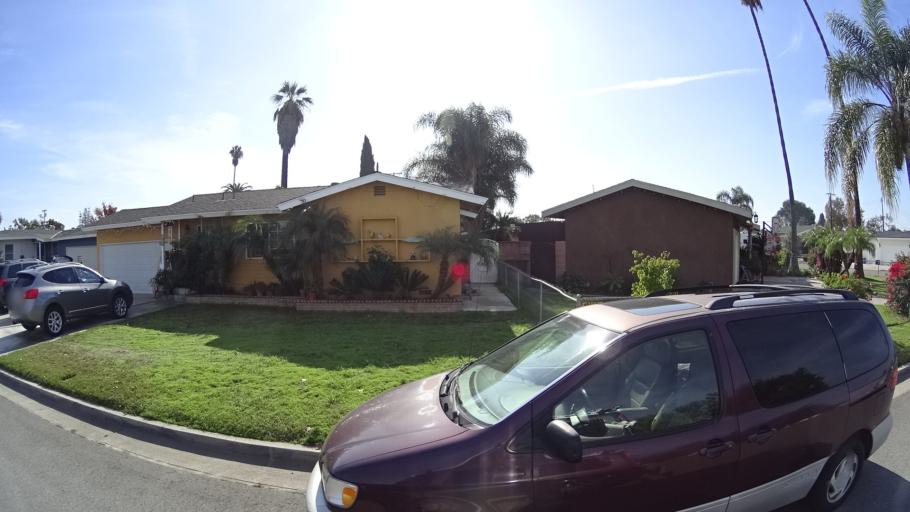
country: US
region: California
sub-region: Orange County
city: Garden Grove
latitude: 33.7900
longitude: -117.9295
